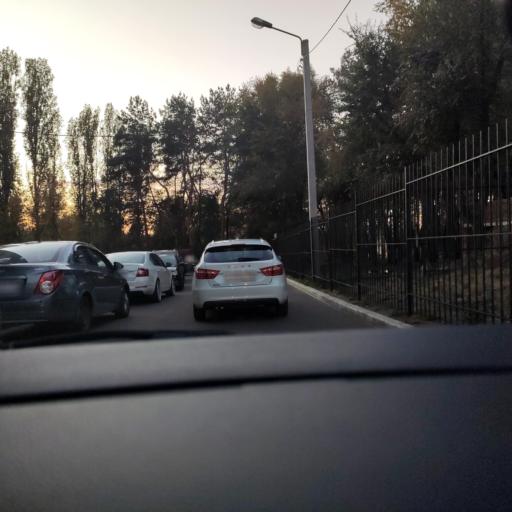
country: RU
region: Voronezj
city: Voronezh
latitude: 51.6848
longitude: 39.2540
